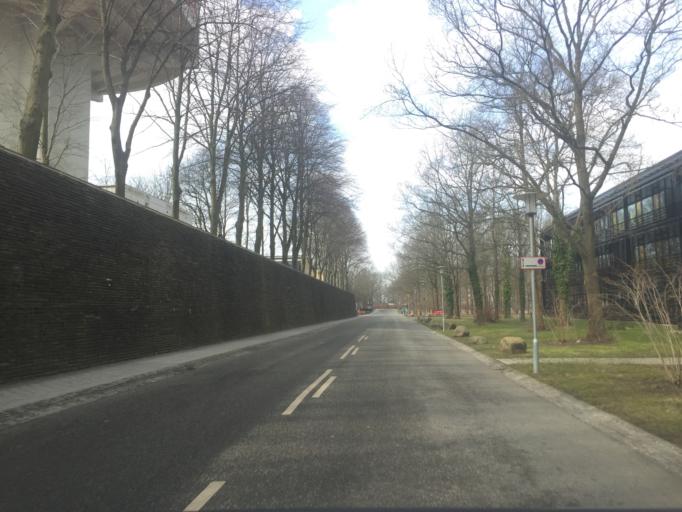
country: DK
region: Capital Region
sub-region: Lyngby-Tarbaek Kommune
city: Kongens Lyngby
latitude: 55.7829
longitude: 12.5164
